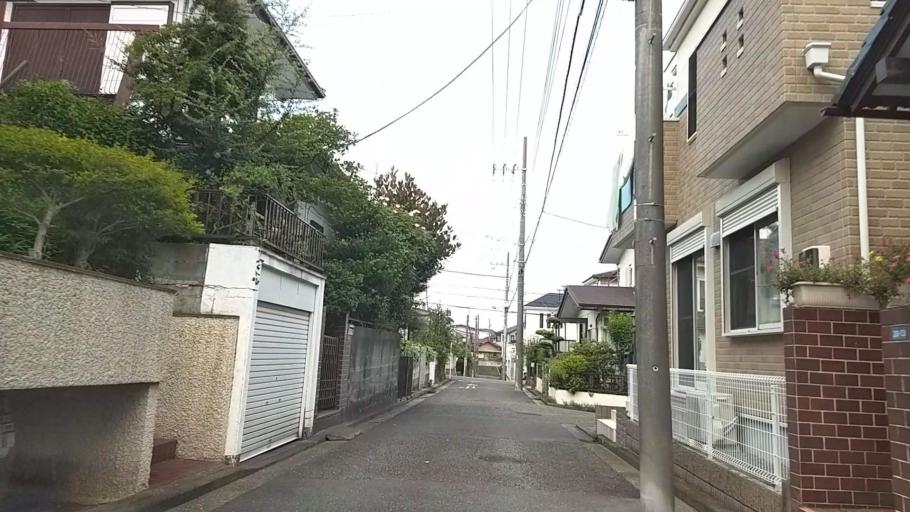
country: JP
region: Kanagawa
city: Yokohama
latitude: 35.4127
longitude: 139.5751
